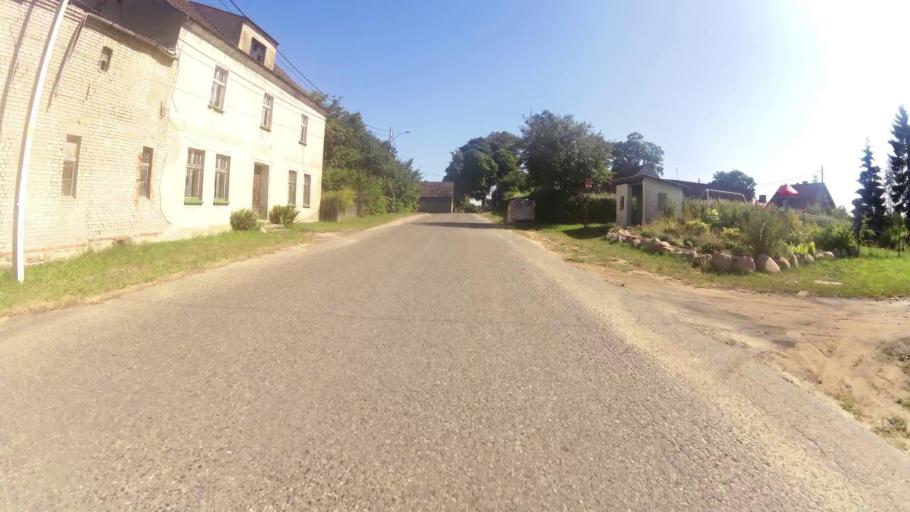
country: PL
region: West Pomeranian Voivodeship
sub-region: Powiat stargardzki
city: Insko
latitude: 53.4435
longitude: 15.6451
